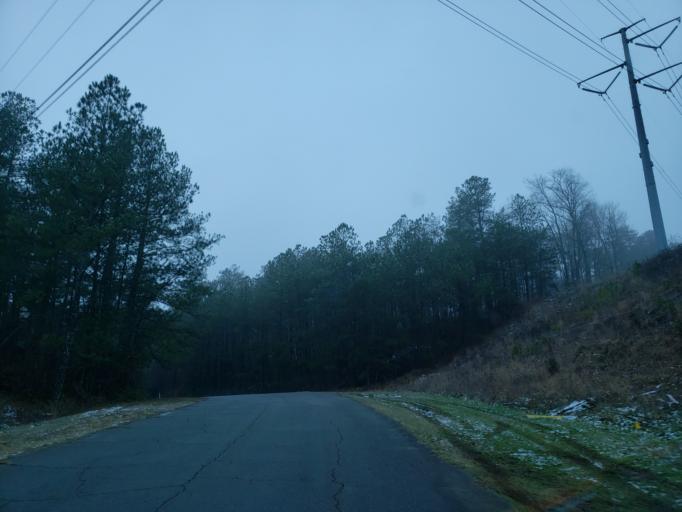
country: US
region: Georgia
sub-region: Cobb County
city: Marietta
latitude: 33.9968
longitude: -84.5714
